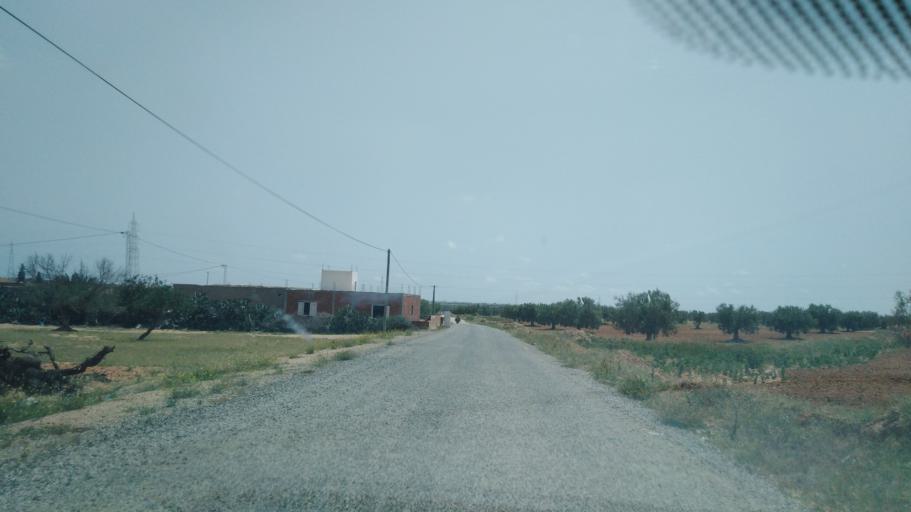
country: TN
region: Safaqis
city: Sfax
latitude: 34.7486
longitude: 10.5710
